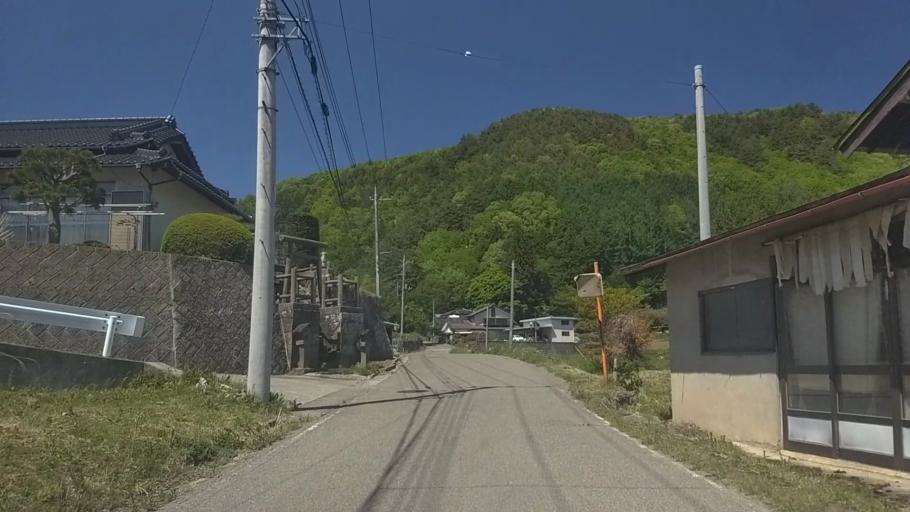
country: JP
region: Yamanashi
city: Nirasaki
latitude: 35.8750
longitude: 138.4533
